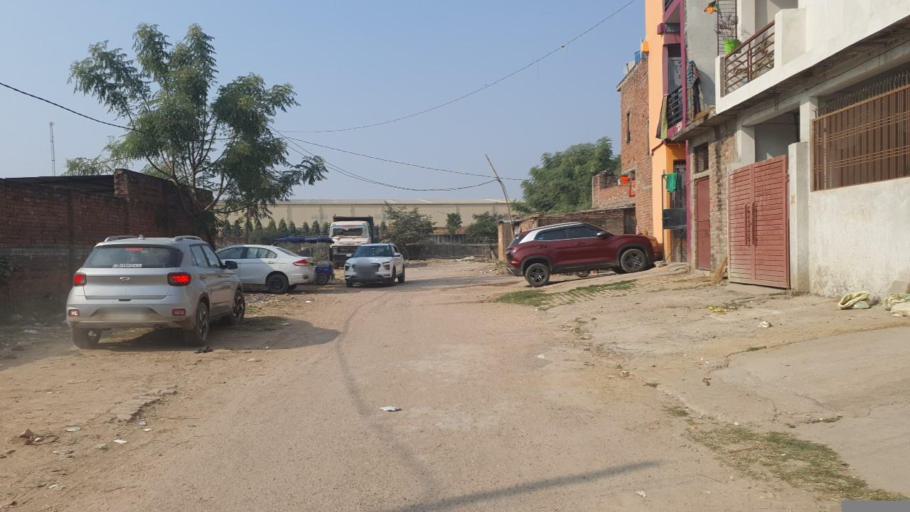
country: IN
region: Uttar Pradesh
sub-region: Lucknow District
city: Lucknow
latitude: 26.7986
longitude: 81.0053
